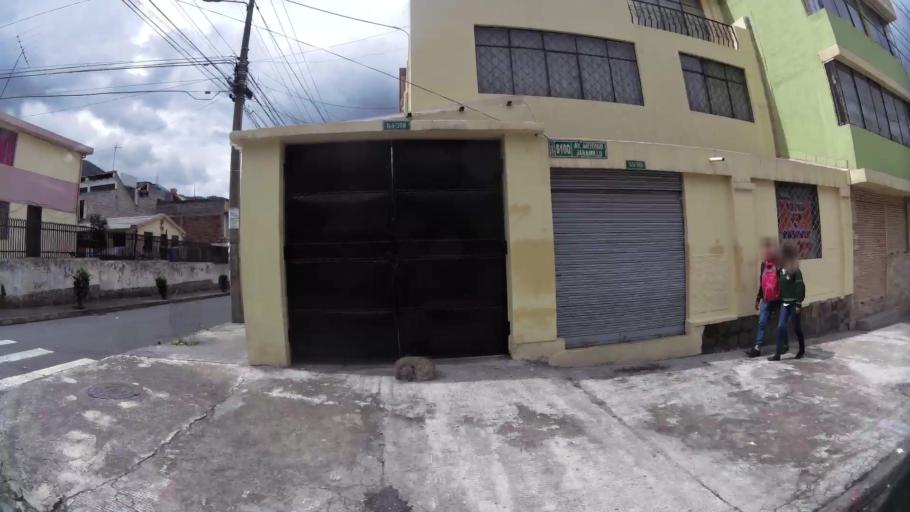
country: EC
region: Pichincha
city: Quito
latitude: -0.2467
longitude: -78.5332
